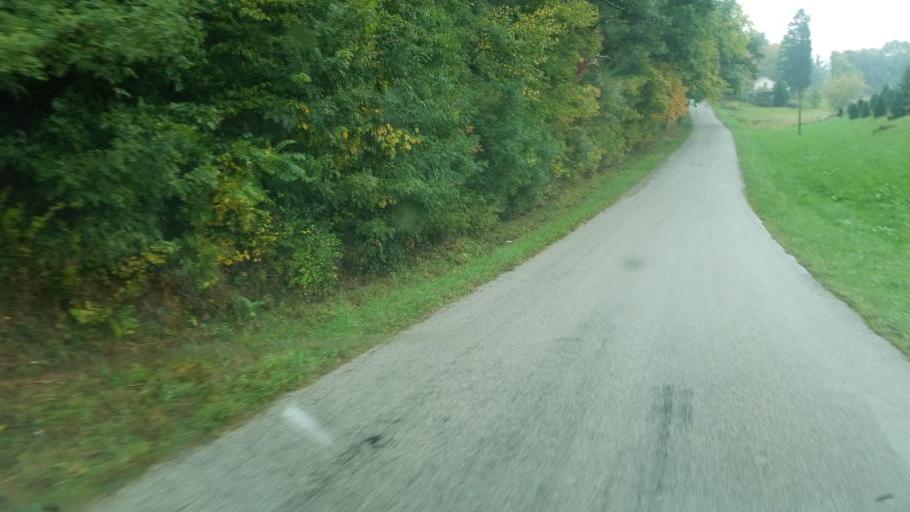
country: US
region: Ohio
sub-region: Sandusky County
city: Bellville
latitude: 40.5783
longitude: -82.4759
